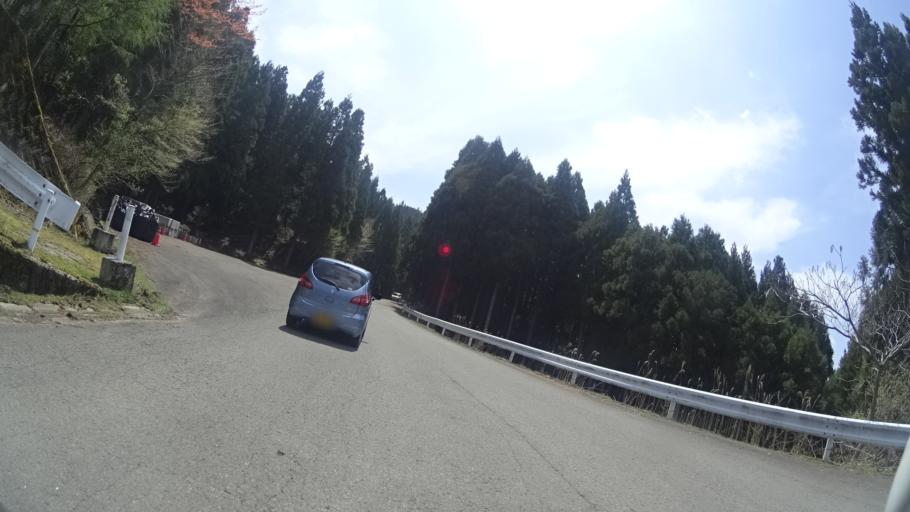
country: JP
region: Tokushima
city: Wakimachi
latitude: 33.8815
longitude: 134.0565
